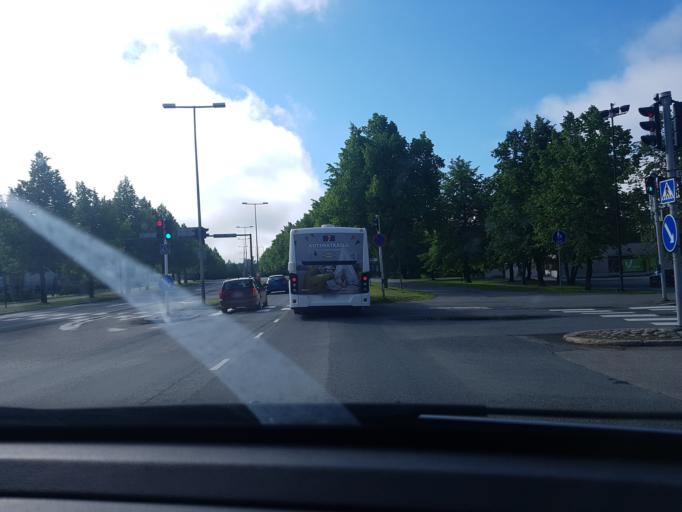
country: FI
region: Northern Savo
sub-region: Kuopio
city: Kuopio
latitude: 62.8992
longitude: 27.6637
